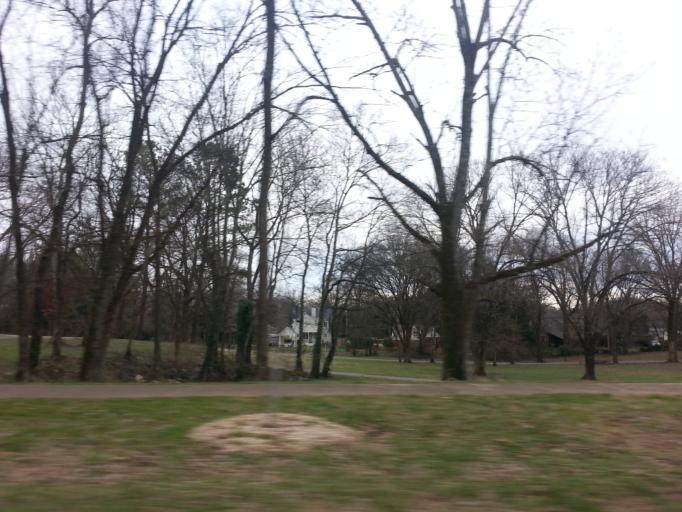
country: US
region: Tennessee
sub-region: Knox County
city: Knoxville
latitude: 35.9338
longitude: -83.9679
